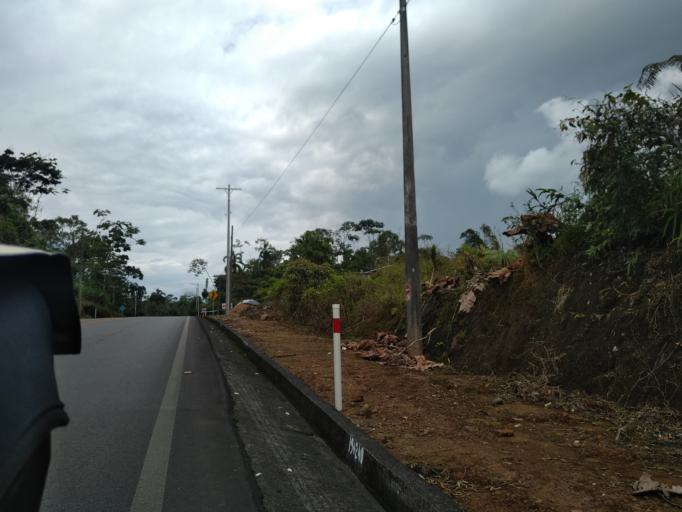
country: EC
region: Pastaza
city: Puyo
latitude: -1.3346
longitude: -77.9040
